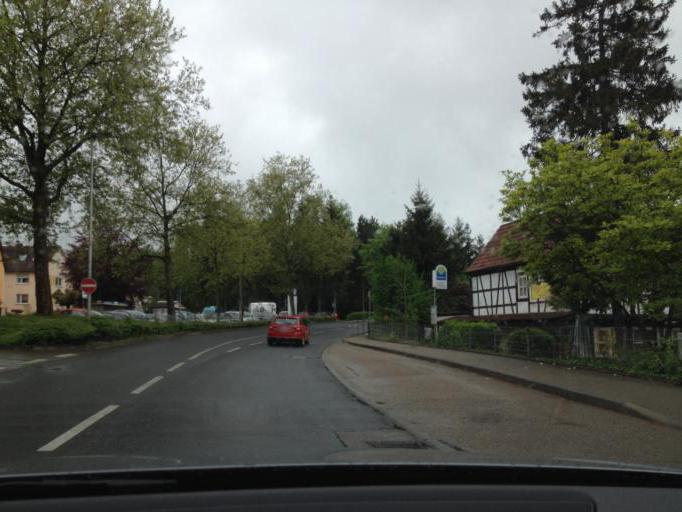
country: DE
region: Baden-Wuerttemberg
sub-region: Regierungsbezirk Stuttgart
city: Bad Wimpfen
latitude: 49.2275
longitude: 9.1622
